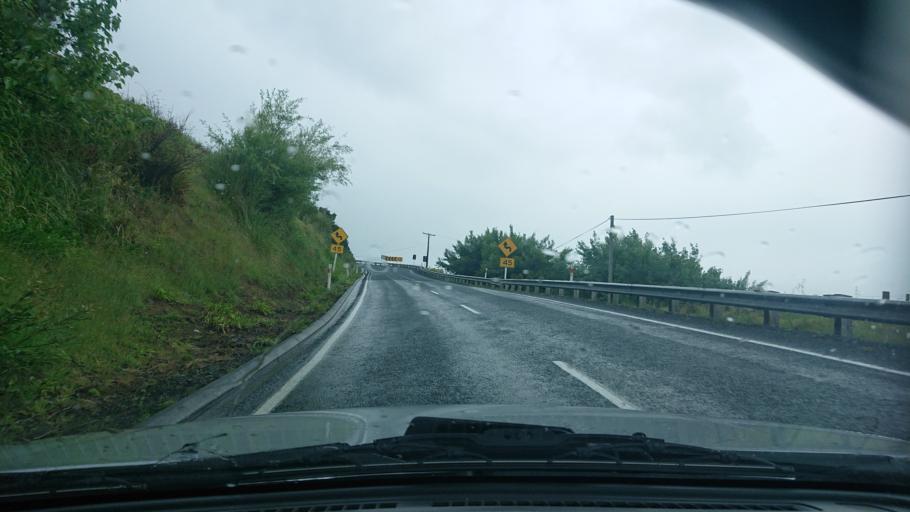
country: NZ
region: Auckland
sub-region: Auckland
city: Wellsford
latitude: -36.3464
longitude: 174.4748
